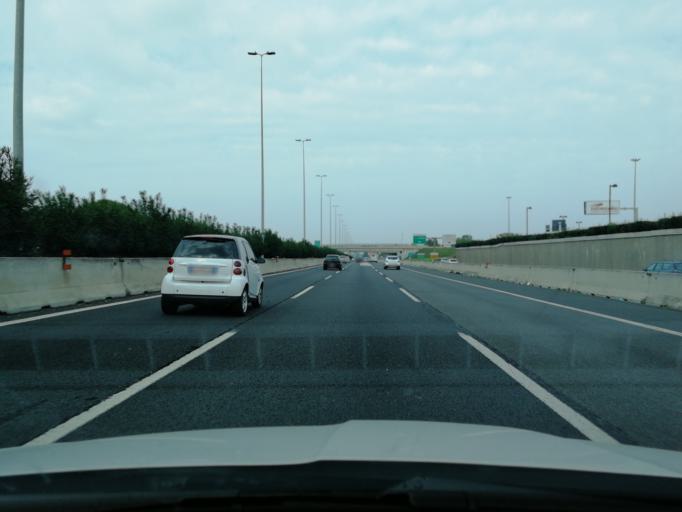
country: IT
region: Latium
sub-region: Citta metropolitana di Roma Capitale
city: Ciampino
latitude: 41.8502
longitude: 12.5966
